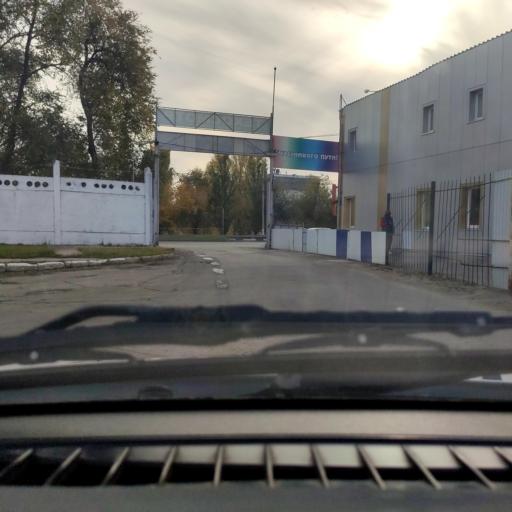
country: RU
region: Samara
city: Zhigulevsk
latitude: 53.4871
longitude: 49.4806
